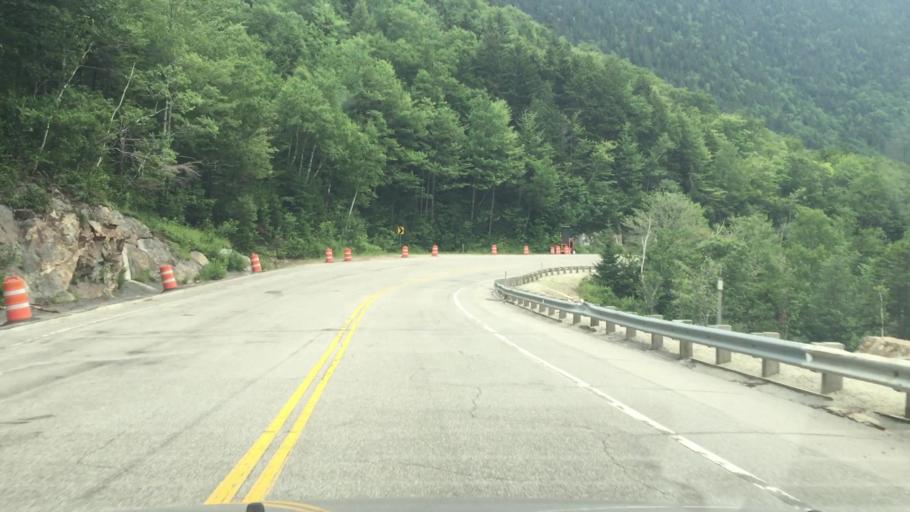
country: US
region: New Hampshire
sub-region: Grafton County
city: Deerfield
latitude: 44.2117
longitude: -71.4051
